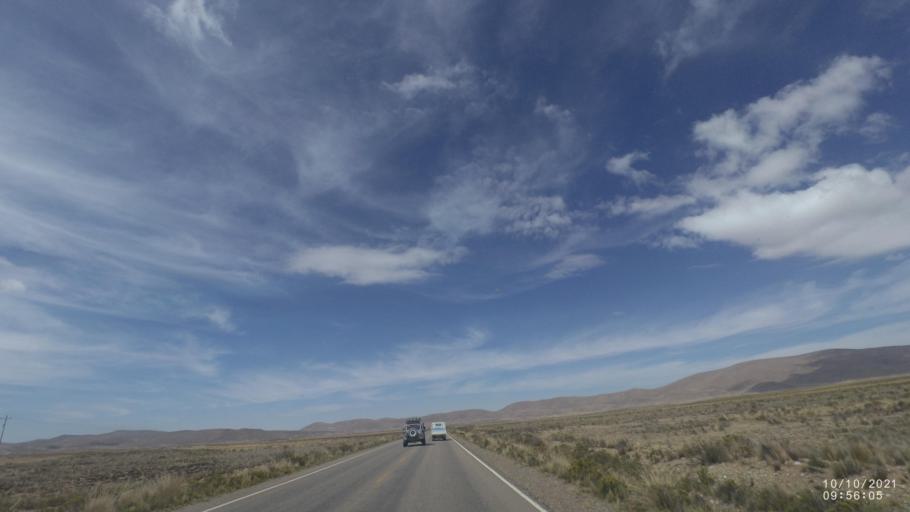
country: BO
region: La Paz
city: Colquiri
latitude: -17.3174
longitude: -67.3717
